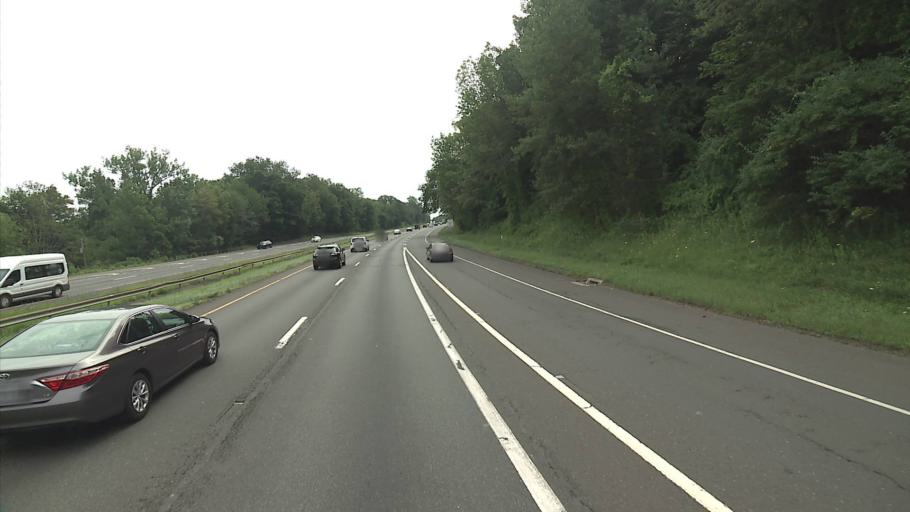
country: US
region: Connecticut
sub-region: Fairfield County
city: Newtown
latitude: 41.4256
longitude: -73.3519
